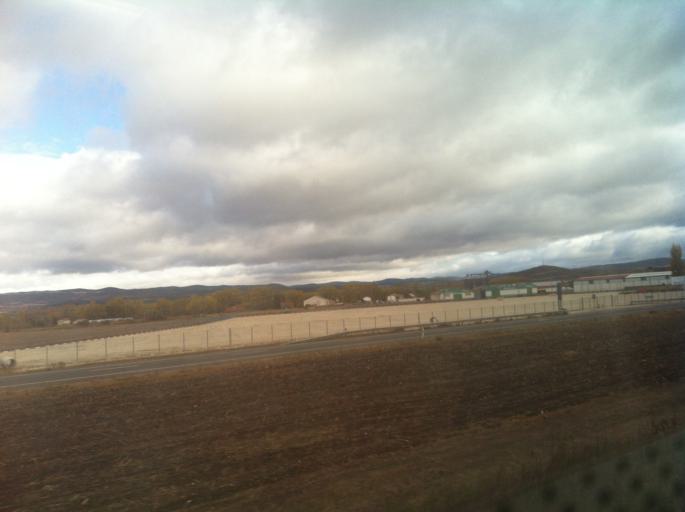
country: ES
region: Castille and Leon
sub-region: Provincia de Burgos
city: Miranda de Ebro
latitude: 42.6844
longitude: -2.9695
